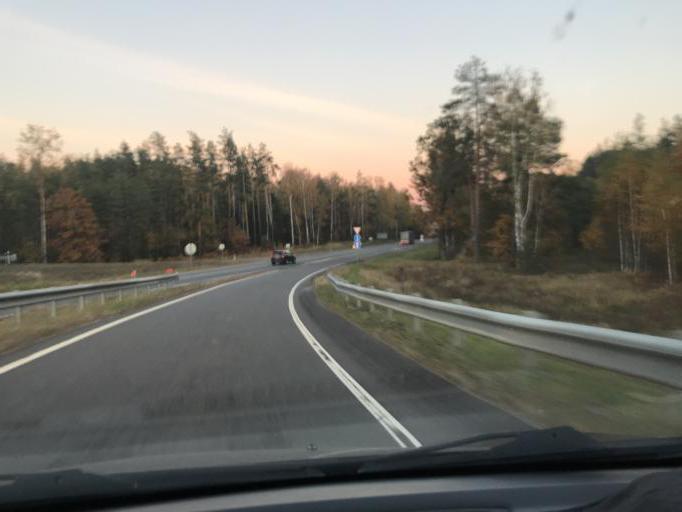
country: BY
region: Mogilev
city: Babruysk
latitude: 53.2084
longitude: 29.0745
